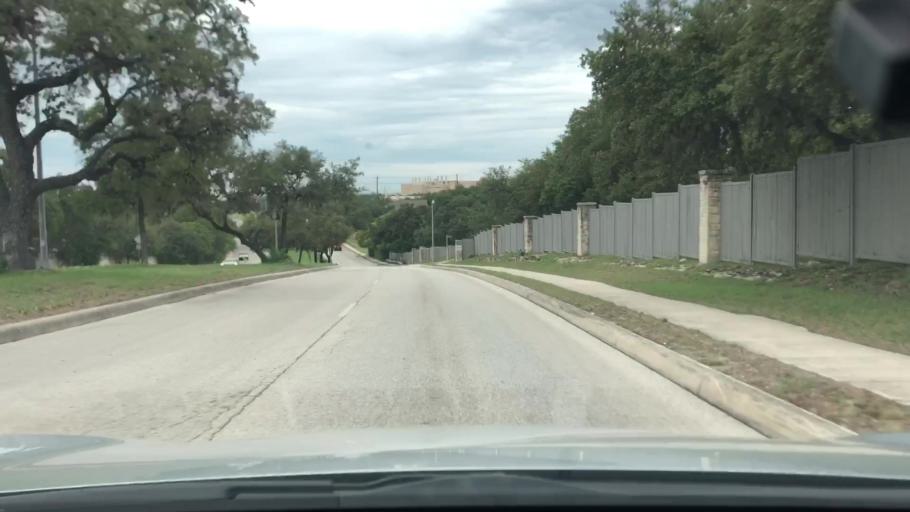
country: US
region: Texas
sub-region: Bexar County
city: Leon Valley
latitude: 29.4651
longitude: -98.6742
